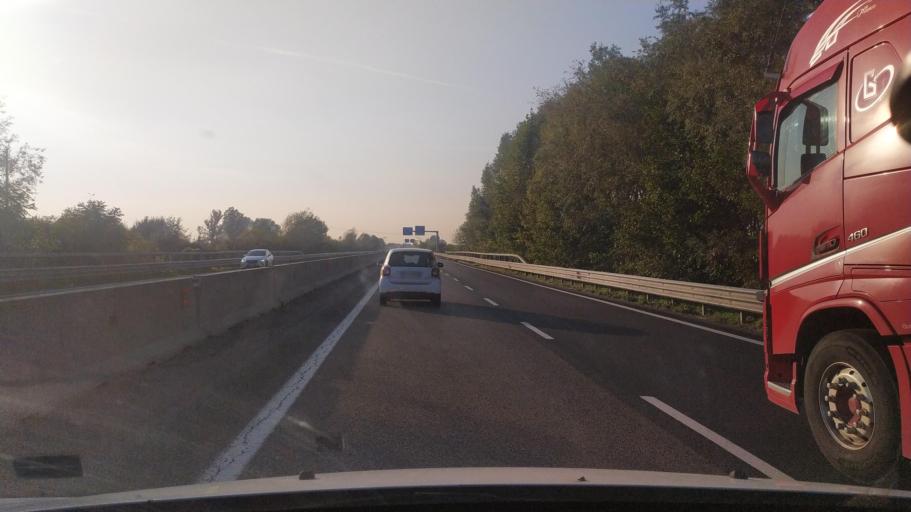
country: IT
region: Lombardy
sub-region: Provincia di Cremona
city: Palazzo Pignano
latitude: 45.3842
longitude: 9.5574
